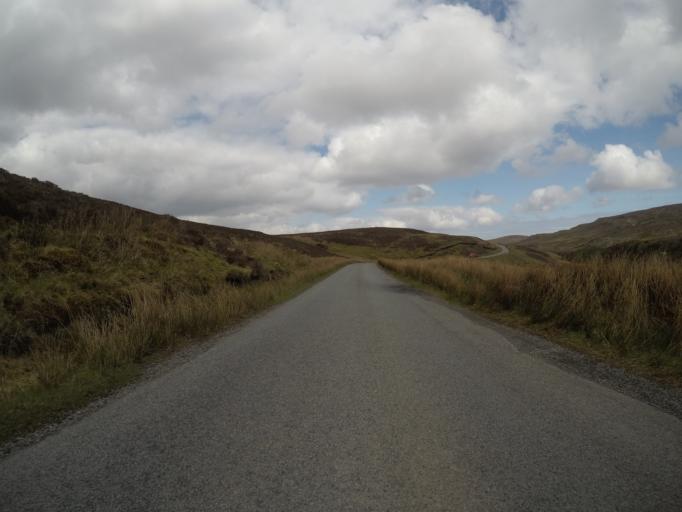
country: GB
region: Scotland
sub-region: Highland
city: Isle of Skye
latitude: 57.3801
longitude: -6.3642
